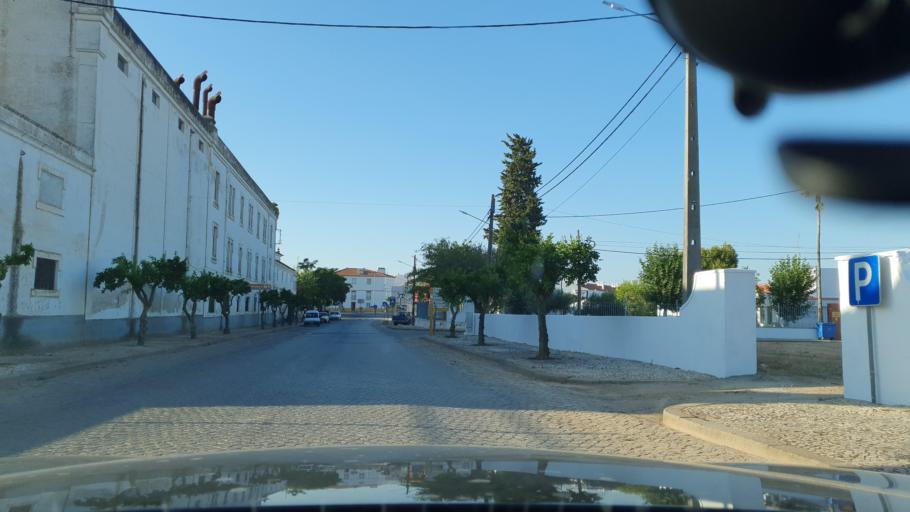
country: PT
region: Portalegre
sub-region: Fronteira
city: Fronteira
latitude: 38.9490
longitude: -7.6757
